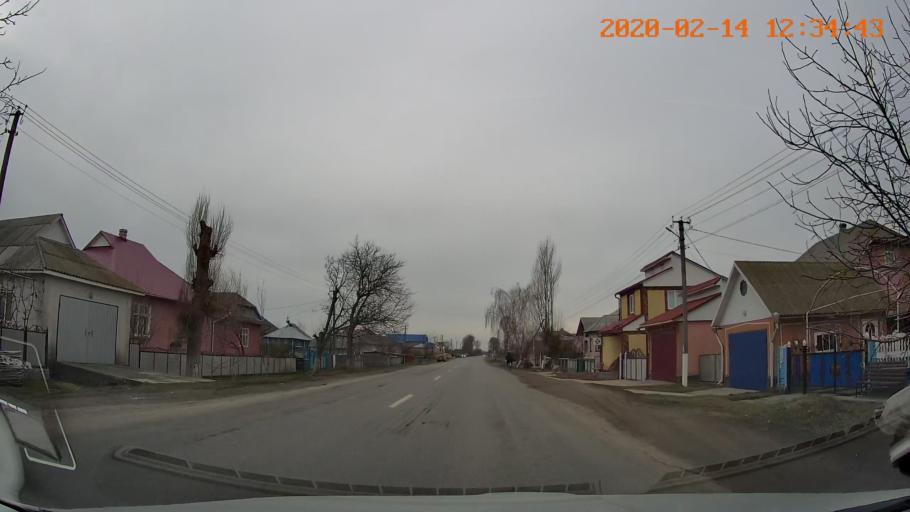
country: RO
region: Botosani
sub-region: Comuna Darabani
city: Bajura
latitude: 48.2283
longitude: 26.5254
